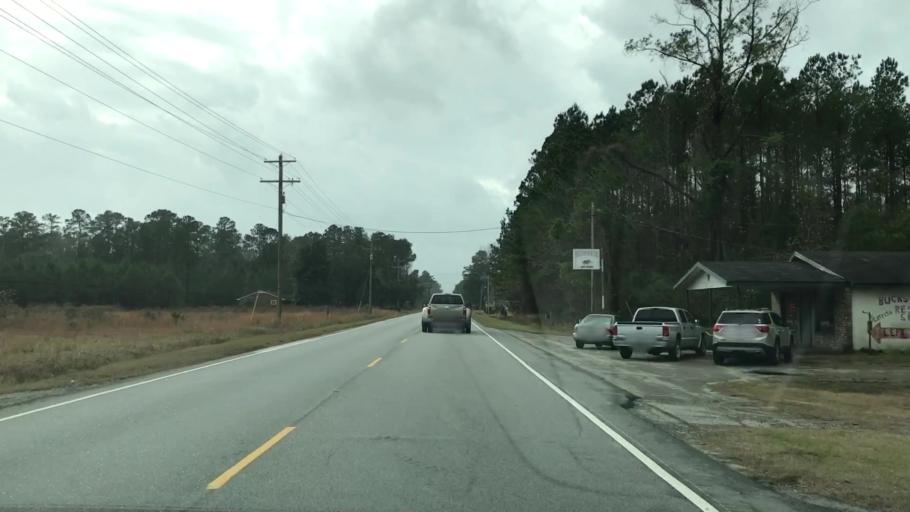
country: US
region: South Carolina
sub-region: Horry County
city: Socastee
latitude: 33.6943
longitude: -79.1146
